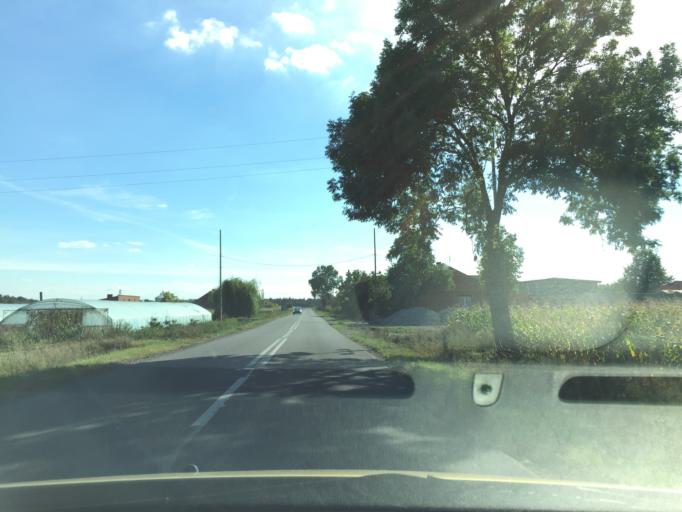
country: PL
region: Greater Poland Voivodeship
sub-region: Powiat kaliski
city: Stawiszyn
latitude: 51.9339
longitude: 18.1478
